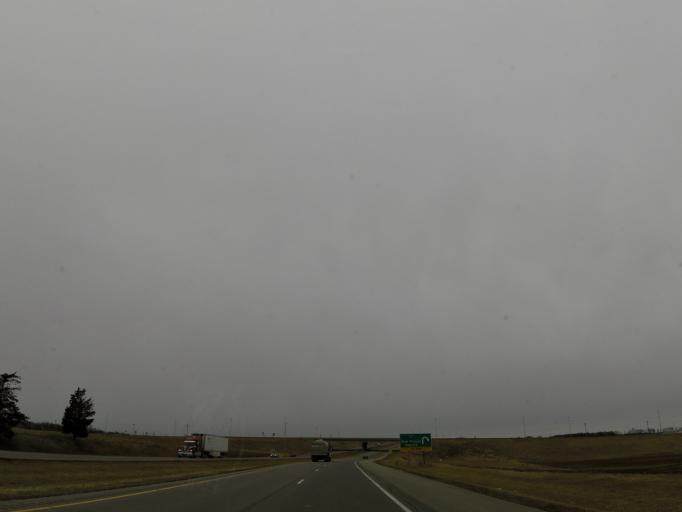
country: US
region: Minnesota
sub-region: Le Sueur County
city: Le Sueur
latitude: 44.5399
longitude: -93.8490
